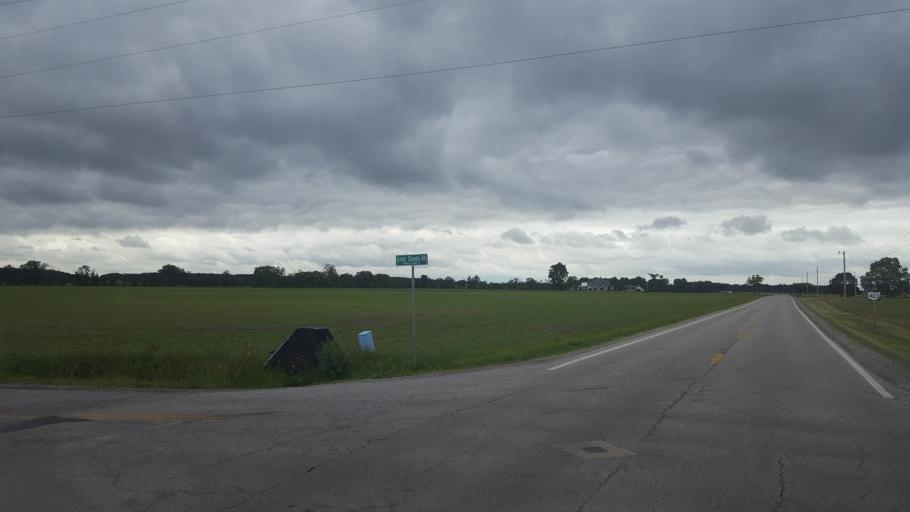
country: US
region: Ohio
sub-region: Marion County
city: Marion
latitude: 40.6590
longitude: -83.1454
